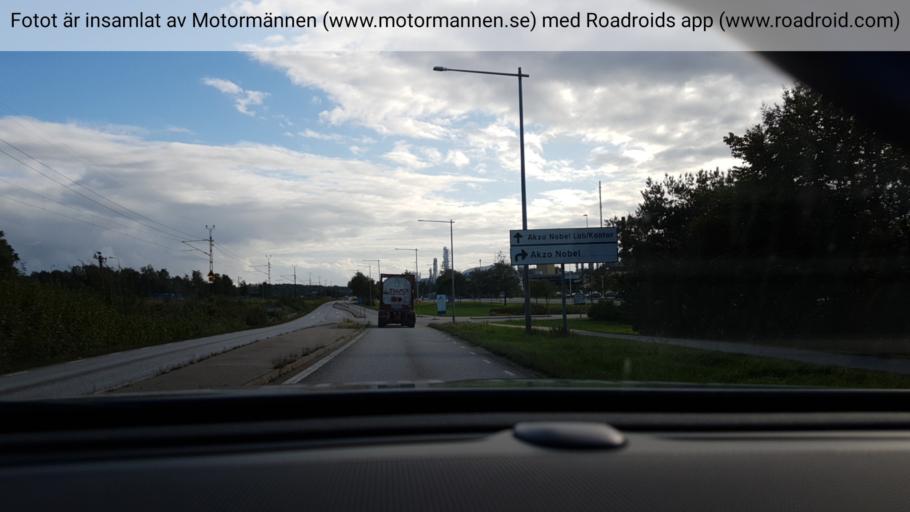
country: SE
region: Vaestra Goetaland
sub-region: Stenungsunds Kommun
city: Stenungsund
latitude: 58.0932
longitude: 11.8345
